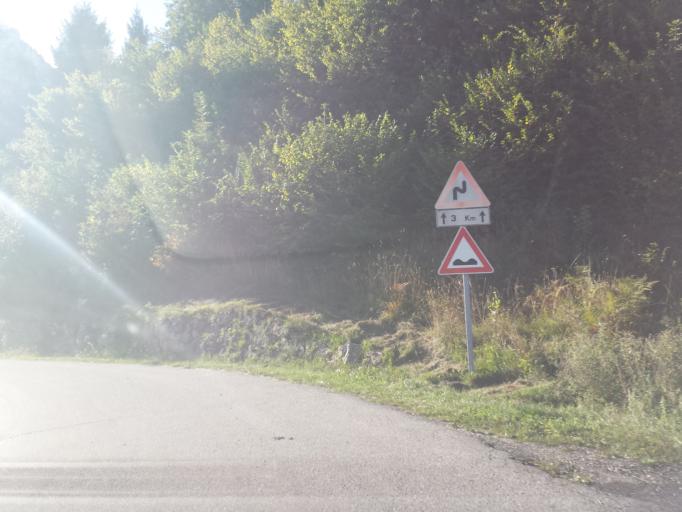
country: IT
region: Veneto
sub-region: Provincia di Vicenza
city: Recoaro Terme
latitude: 45.7193
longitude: 11.1793
